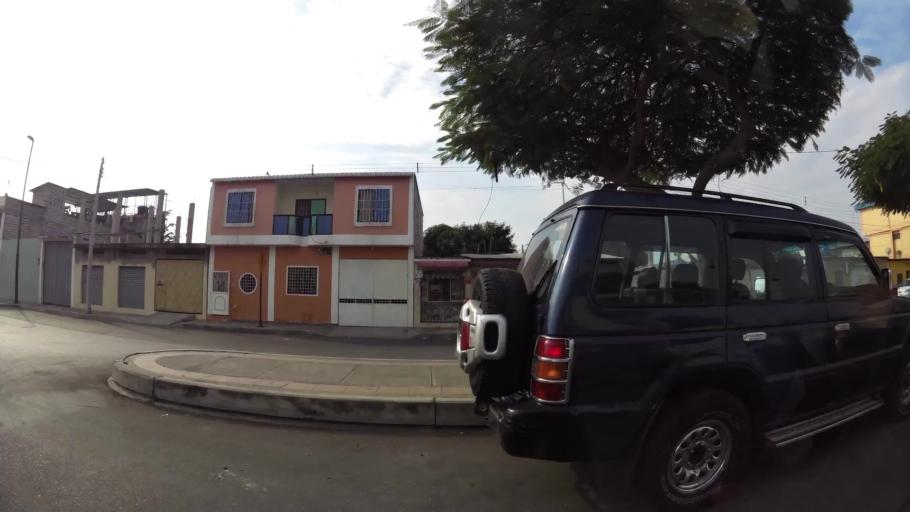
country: EC
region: Guayas
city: Guayaquil
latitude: -2.2452
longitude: -79.9069
